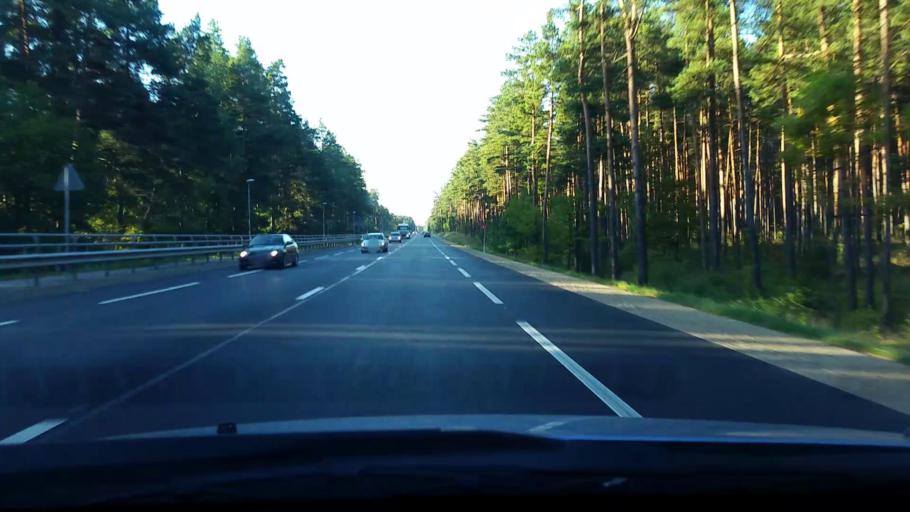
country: LV
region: Adazi
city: Adazi
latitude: 57.0564
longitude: 24.3209
